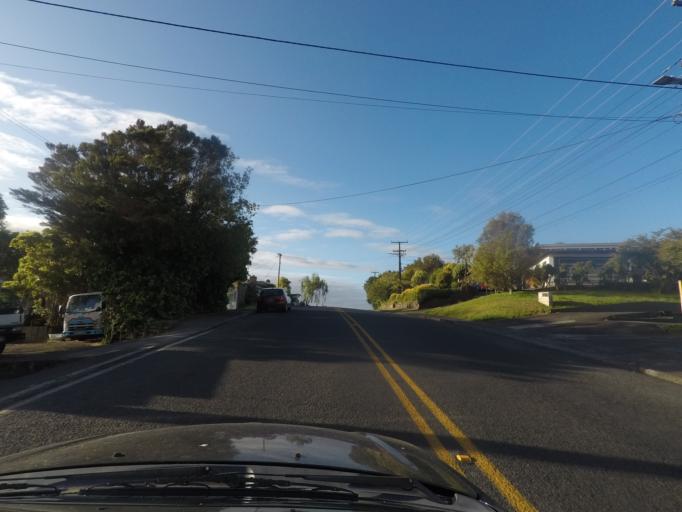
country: NZ
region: Auckland
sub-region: Auckland
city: Waitakere
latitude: -36.9179
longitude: 174.6578
